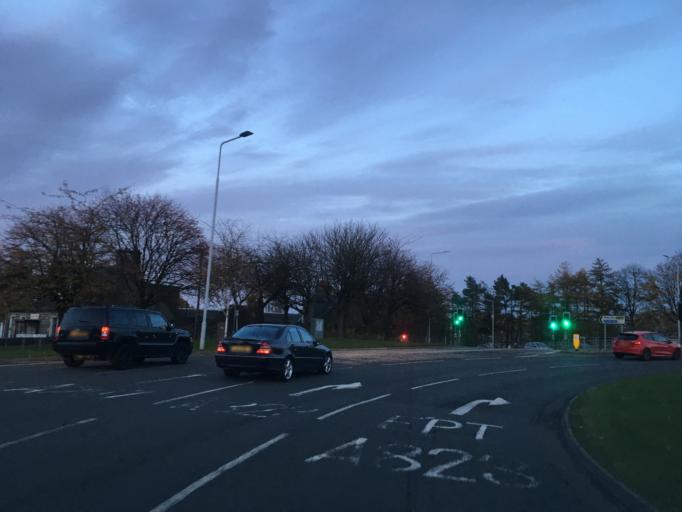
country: GB
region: Scotland
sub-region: Fife
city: Dunfermline
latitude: 56.0730
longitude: -3.4530
